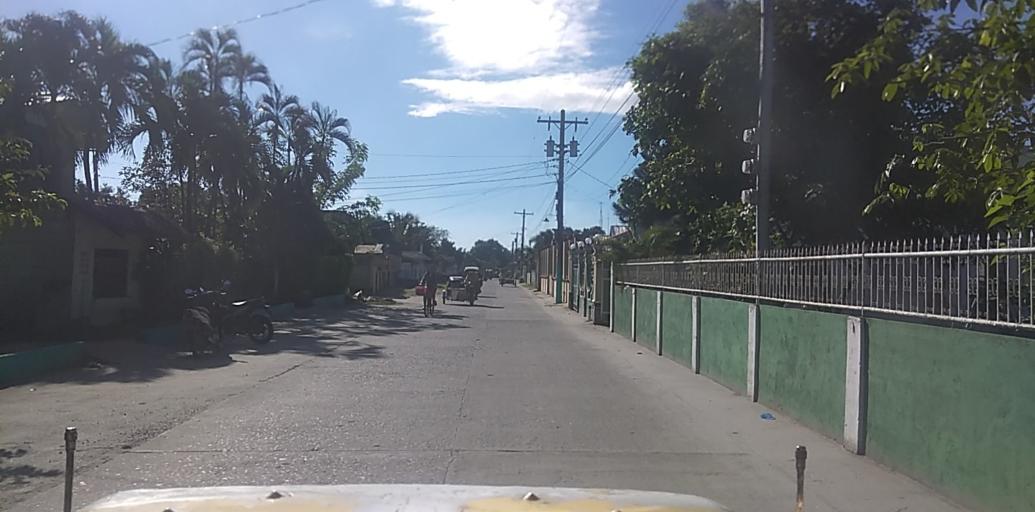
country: PH
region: Central Luzon
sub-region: Province of Pampanga
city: San Patricio
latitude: 15.1087
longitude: 120.7124
